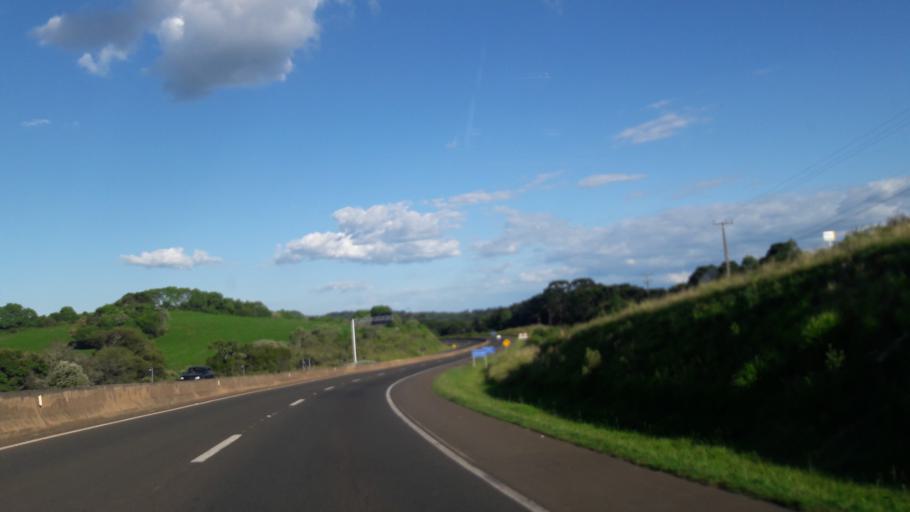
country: BR
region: Parana
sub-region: Guarapuava
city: Guarapuava
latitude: -25.3391
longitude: -51.4273
